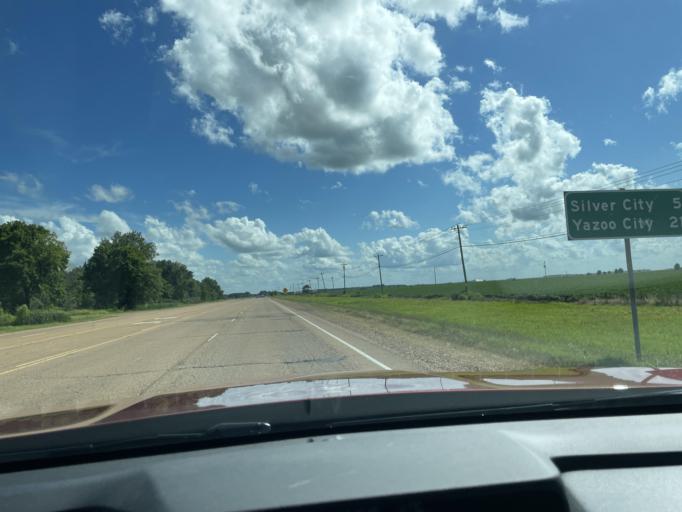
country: US
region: Mississippi
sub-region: Humphreys County
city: Belzoni
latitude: 33.1588
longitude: -90.5017
